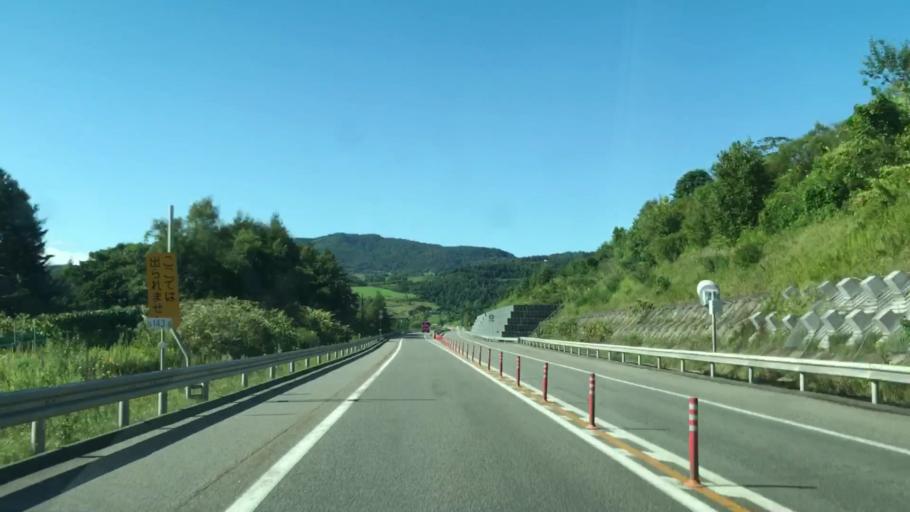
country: JP
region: Hokkaido
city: Date
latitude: 42.5407
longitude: 140.7952
